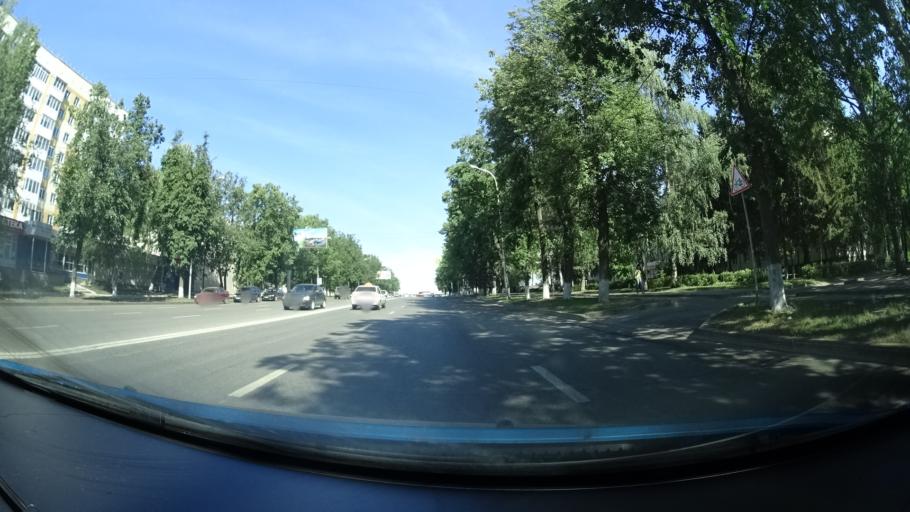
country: RU
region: Bashkortostan
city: Ufa
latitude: 54.7576
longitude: 56.0015
